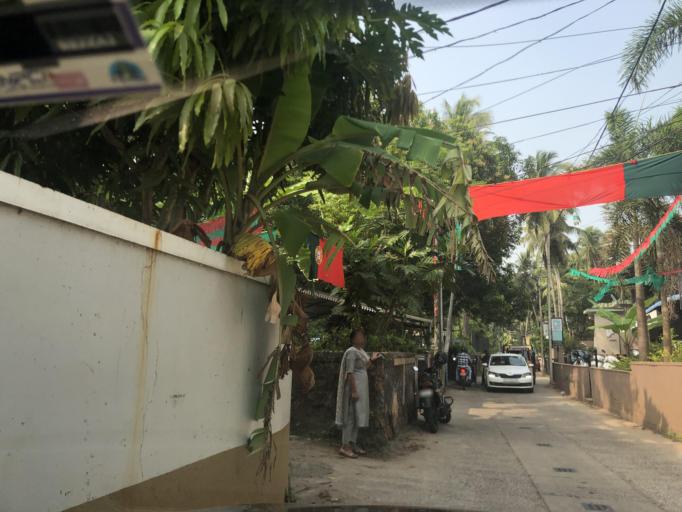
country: IN
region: Kerala
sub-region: Kozhikode
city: Kozhikode
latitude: 11.2799
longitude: 75.7779
